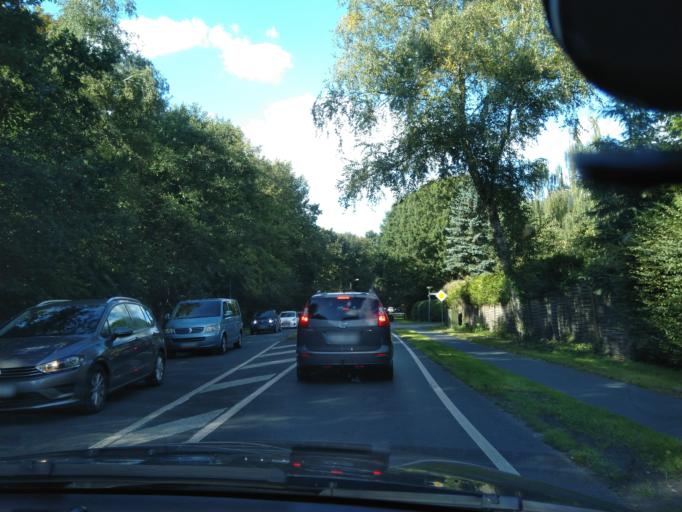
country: DE
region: Lower Saxony
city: Leer
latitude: 53.2516
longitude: 7.4576
